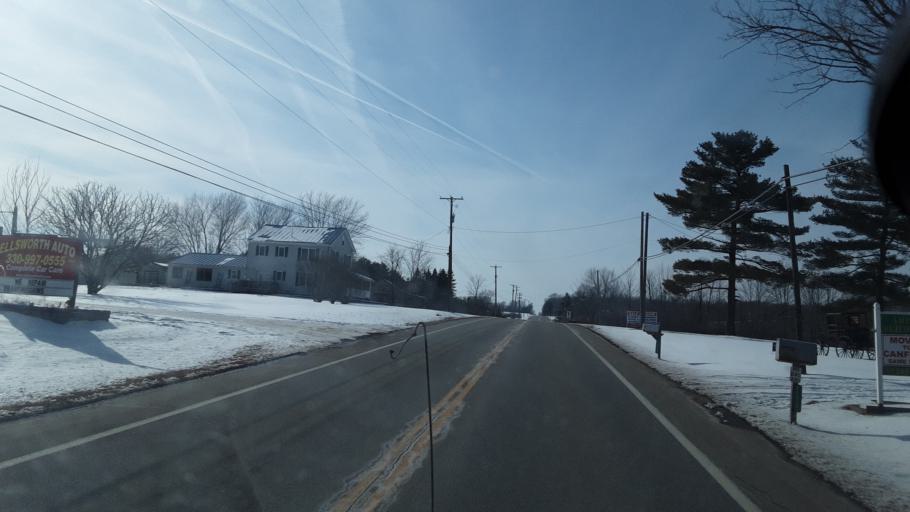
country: US
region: Ohio
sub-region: Mahoning County
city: Canfield
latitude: 41.0244
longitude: -80.8694
